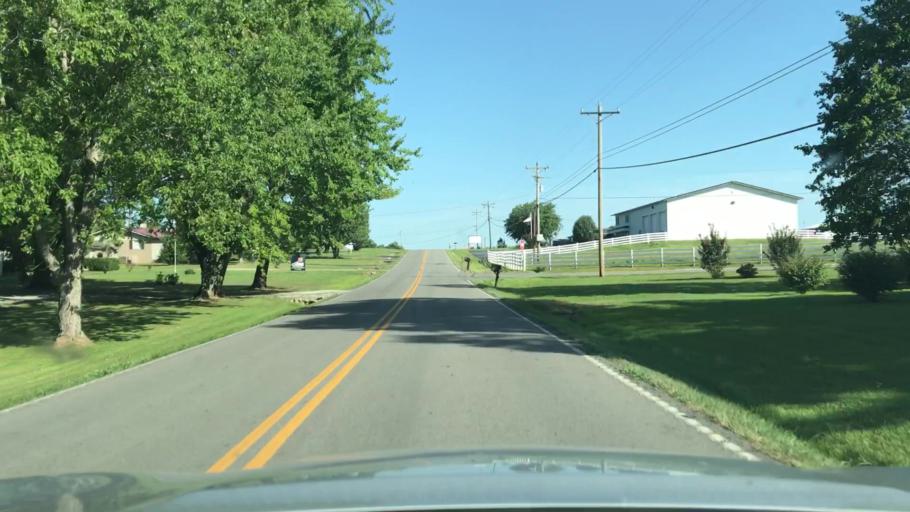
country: US
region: Kentucky
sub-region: Muhlenberg County
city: Greenville
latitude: 37.1638
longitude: -87.1441
